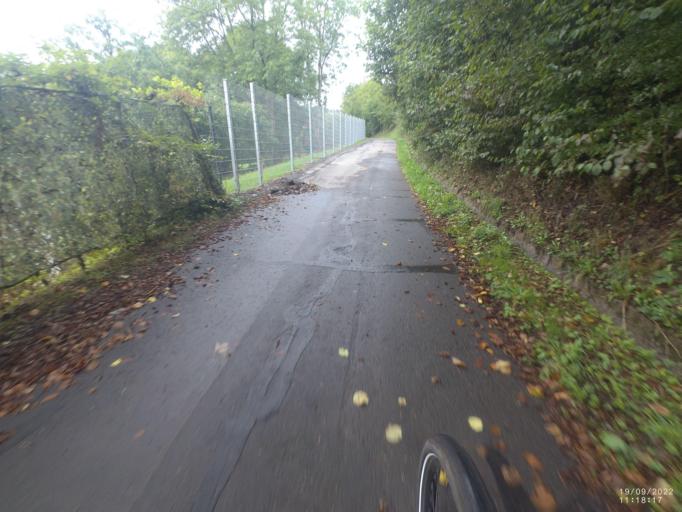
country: DE
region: Rheinland-Pfalz
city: Schutz
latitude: 50.1305
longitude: 6.7551
